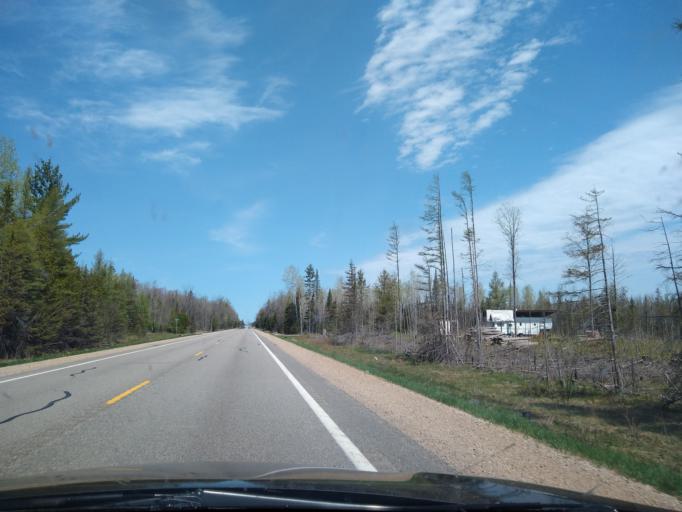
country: US
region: Michigan
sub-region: Delta County
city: Gladstone
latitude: 46.0635
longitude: -86.9812
